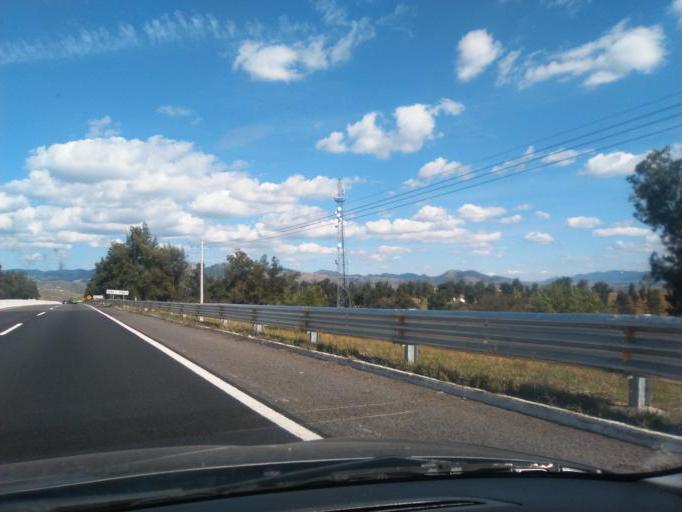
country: MX
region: Guanajuato
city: Santa Teresa
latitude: 20.9659
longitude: -101.3269
